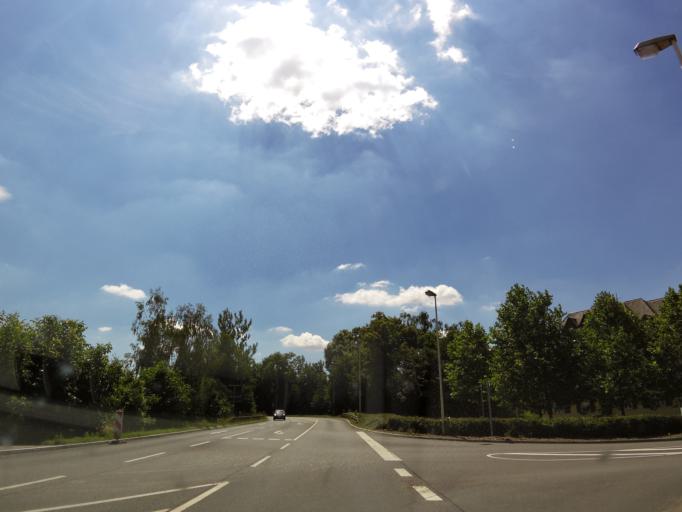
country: DE
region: Saxony
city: Glauchau
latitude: 50.8318
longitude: 12.5211
